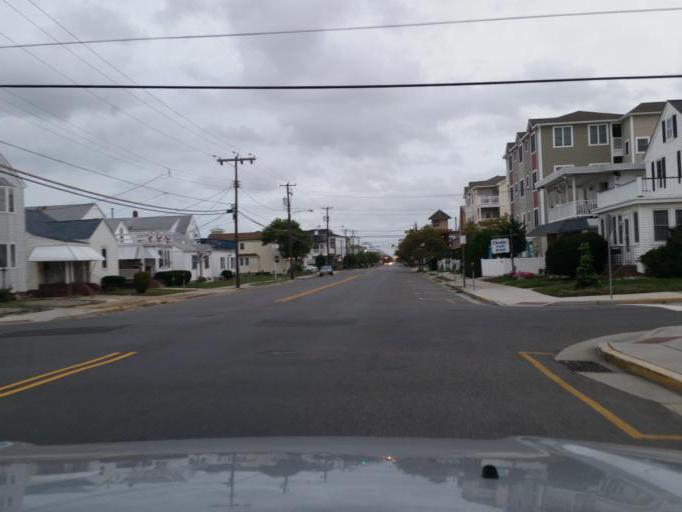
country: US
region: New Jersey
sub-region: Cape May County
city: Wildwood Crest
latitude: 38.9778
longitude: -74.8262
